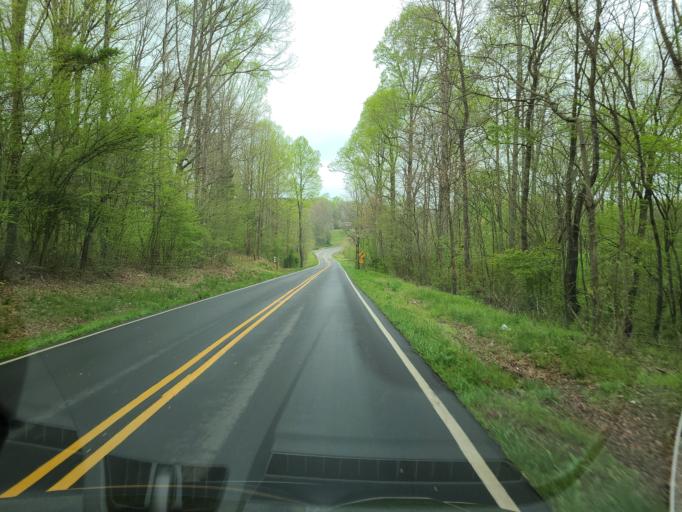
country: US
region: North Carolina
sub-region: Lincoln County
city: Lincolnton
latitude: 35.4587
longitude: -81.3339
